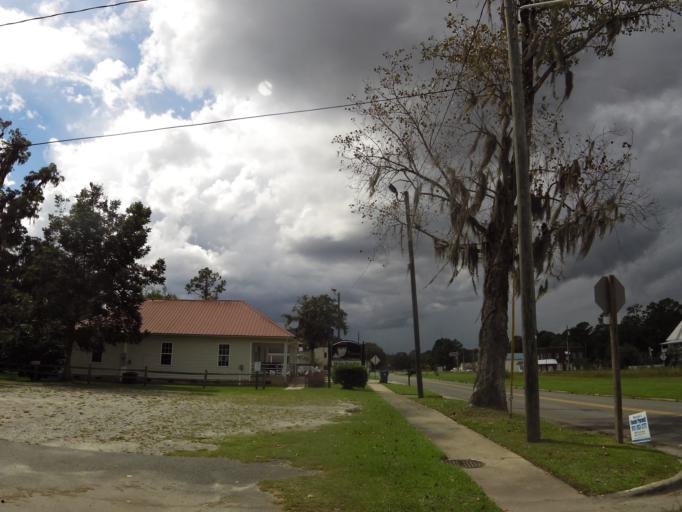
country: US
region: Georgia
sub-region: Brantley County
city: Nahunta
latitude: 31.2044
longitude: -81.9797
